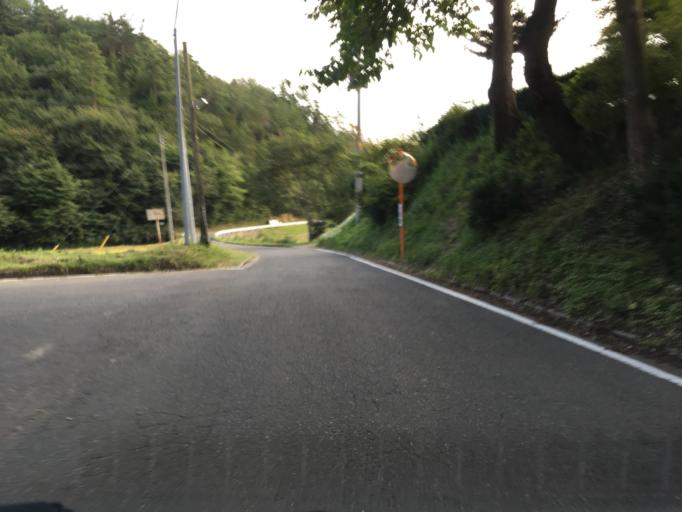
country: JP
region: Fukushima
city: Fukushima-shi
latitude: 37.6869
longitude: 140.5733
